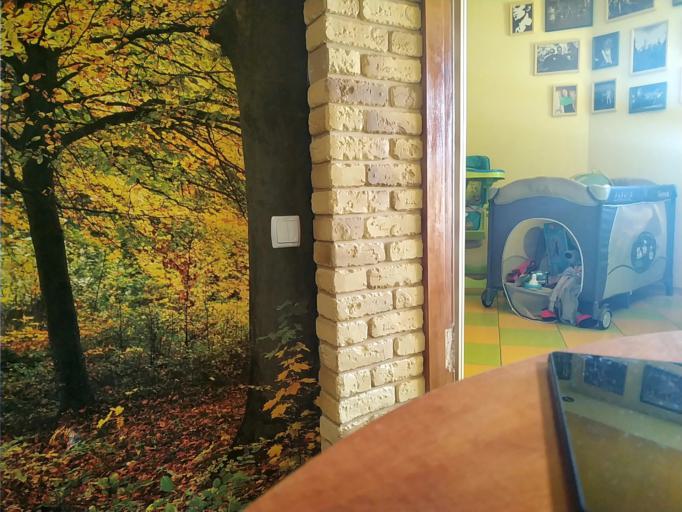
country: RU
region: Tverskaya
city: Vyshniy Volochek
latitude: 57.5897
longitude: 34.5443
